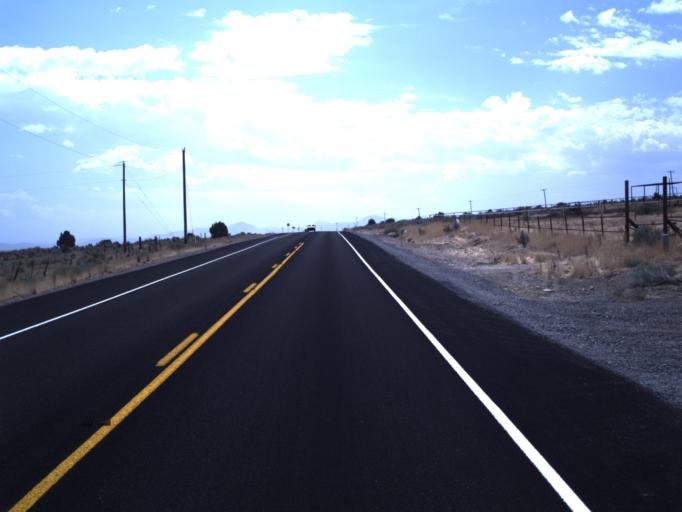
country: US
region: Utah
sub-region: Utah County
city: Eagle Mountain
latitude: 40.3212
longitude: -112.1025
